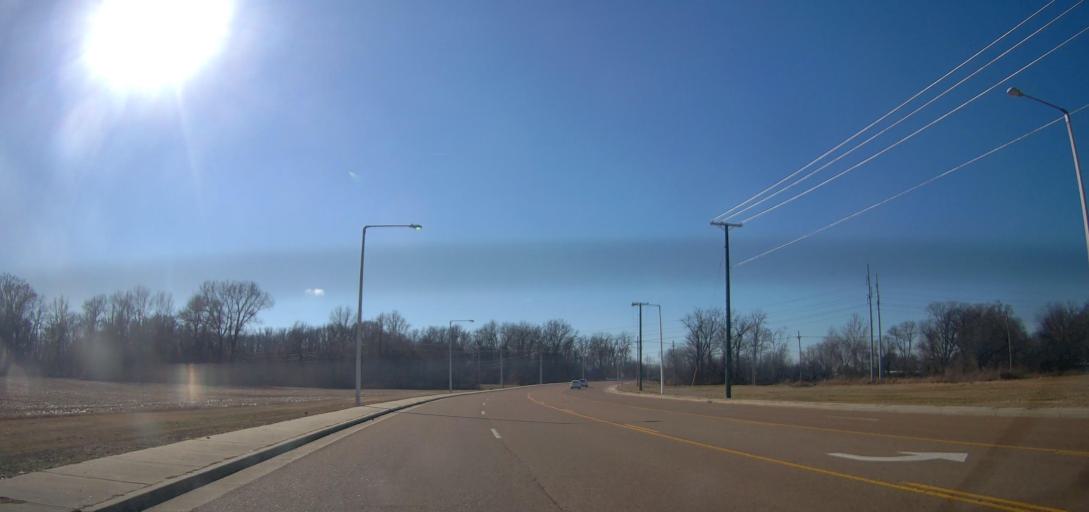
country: US
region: Tennessee
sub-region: Shelby County
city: Millington
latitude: 35.3376
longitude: -89.8901
